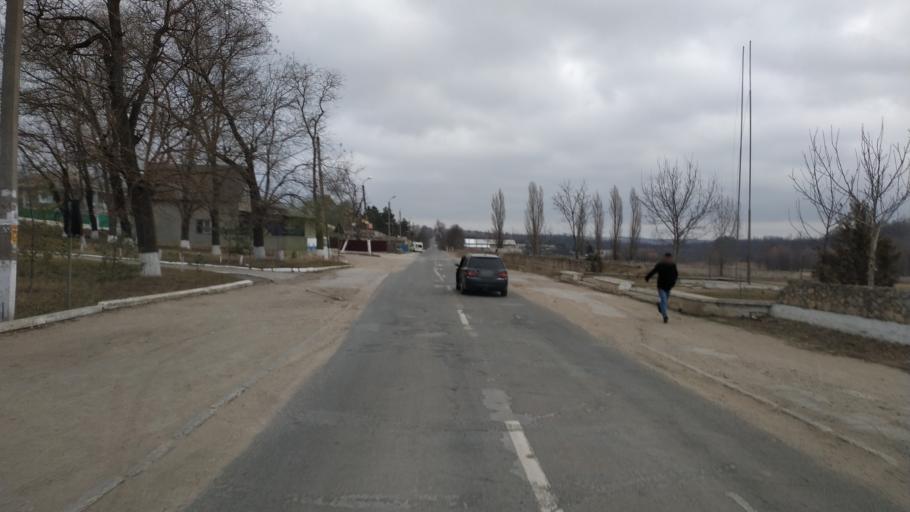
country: MD
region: Laloveni
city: Ialoveni
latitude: 46.9078
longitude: 28.8086
